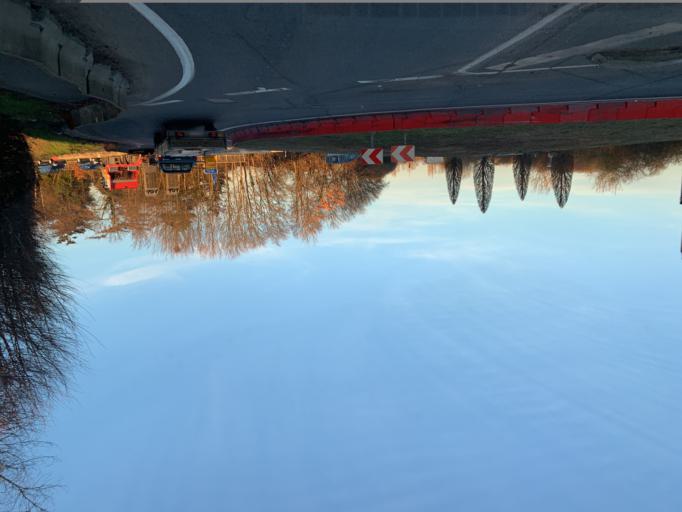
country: DE
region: North Rhine-Westphalia
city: Julich
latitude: 50.9363
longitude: 6.3685
